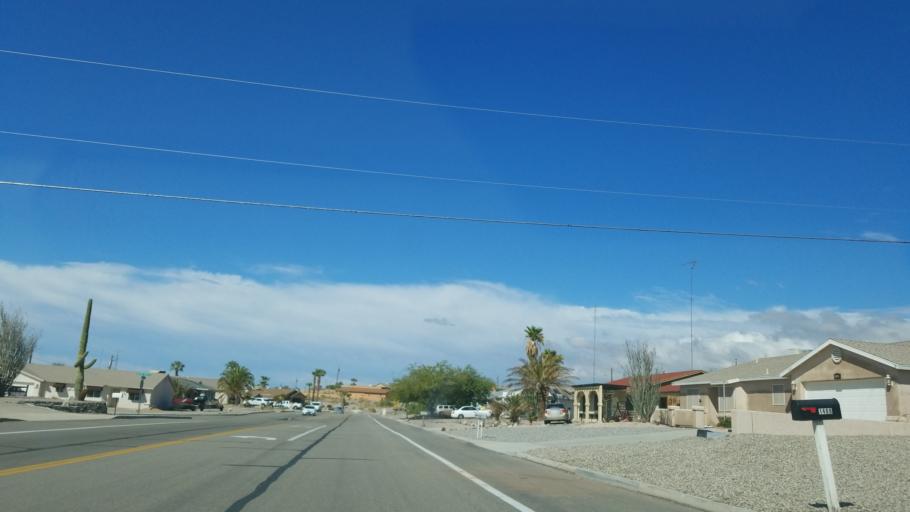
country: US
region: Arizona
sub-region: Mohave County
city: Lake Havasu City
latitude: 34.4602
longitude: -114.2597
